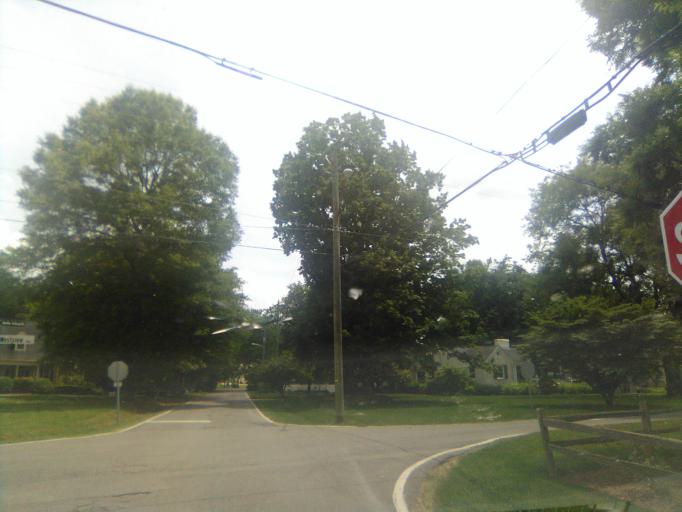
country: US
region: Tennessee
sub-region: Davidson County
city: Belle Meade
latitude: 36.0894
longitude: -86.8527
